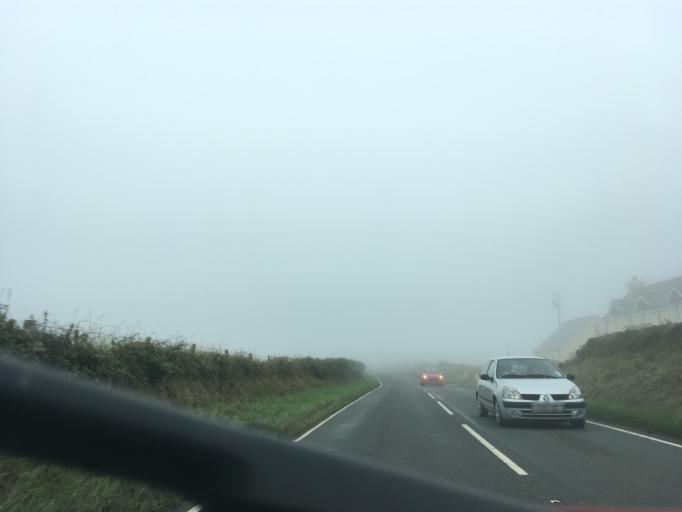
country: GB
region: Wales
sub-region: Pembrokeshire
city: Llanrhian
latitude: 51.8677
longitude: -5.1302
